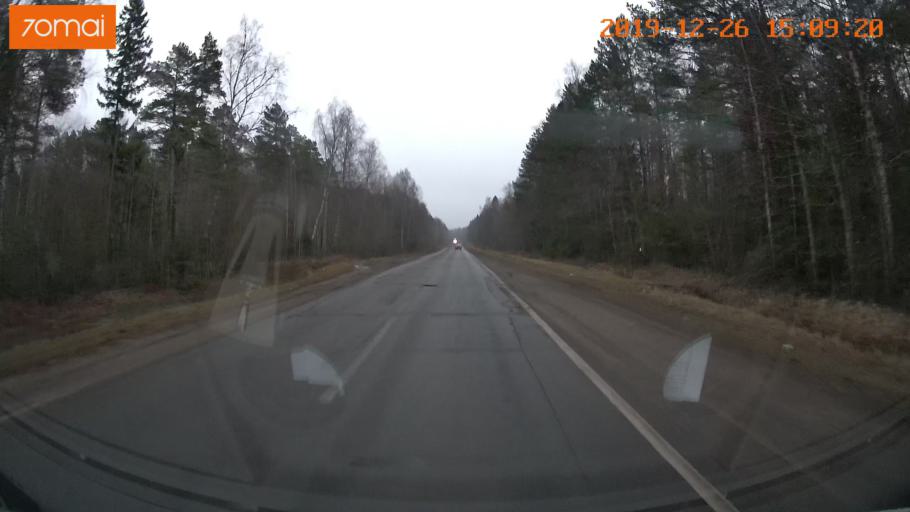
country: RU
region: Jaroslavl
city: Rybinsk
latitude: 58.1501
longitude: 38.8397
